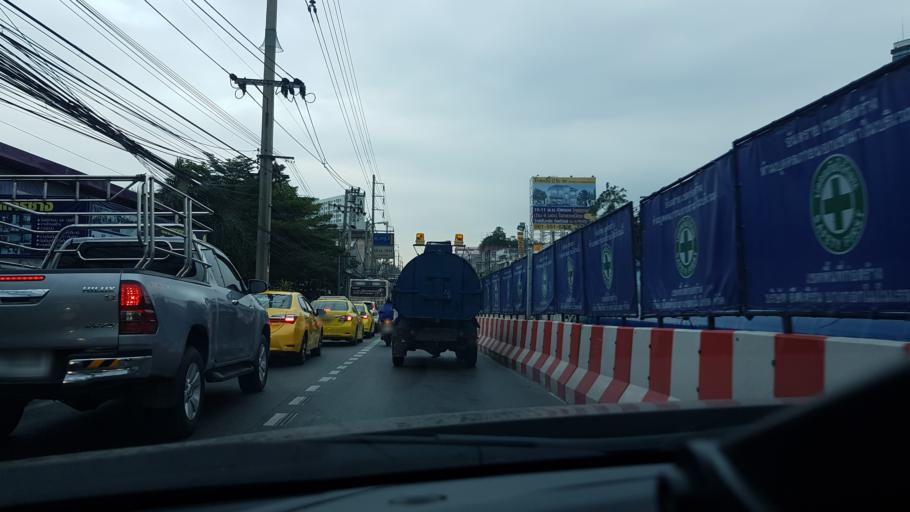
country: TH
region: Bangkok
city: Lat Phrao
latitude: 13.7975
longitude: 100.5893
